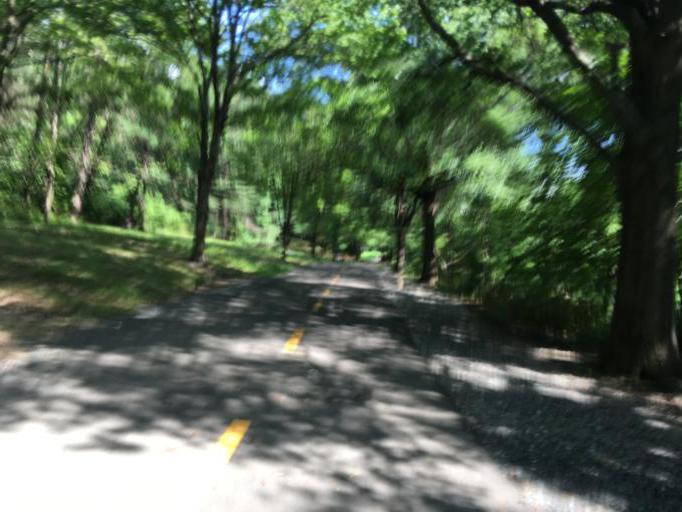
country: US
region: Virginia
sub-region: Fairfax County
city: Rose Hill
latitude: 38.8141
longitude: -77.1159
